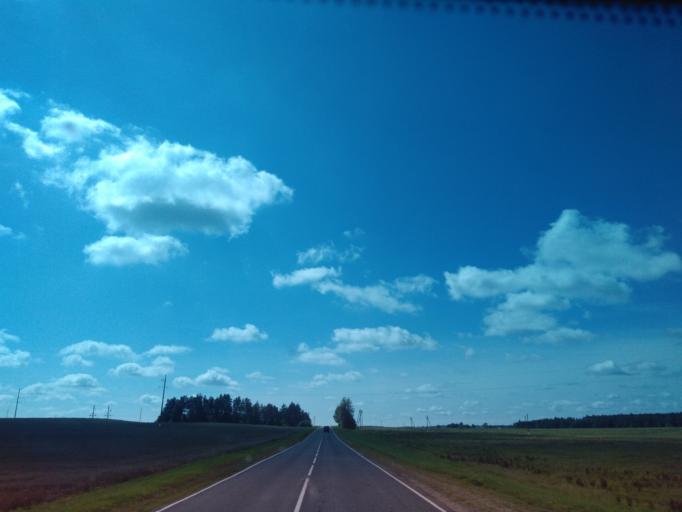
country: BY
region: Minsk
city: Uzda
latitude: 53.3855
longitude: 27.2426
